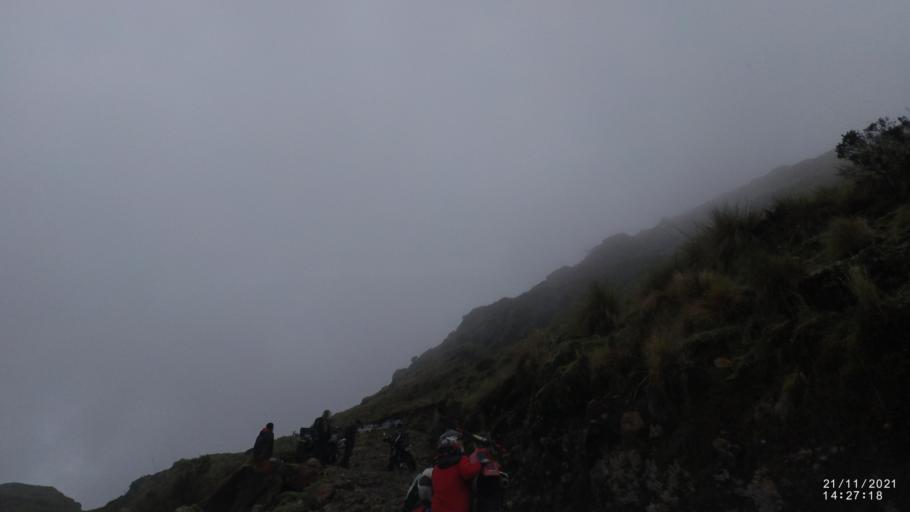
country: BO
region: Cochabamba
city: Cochabamba
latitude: -16.9459
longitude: -66.2575
